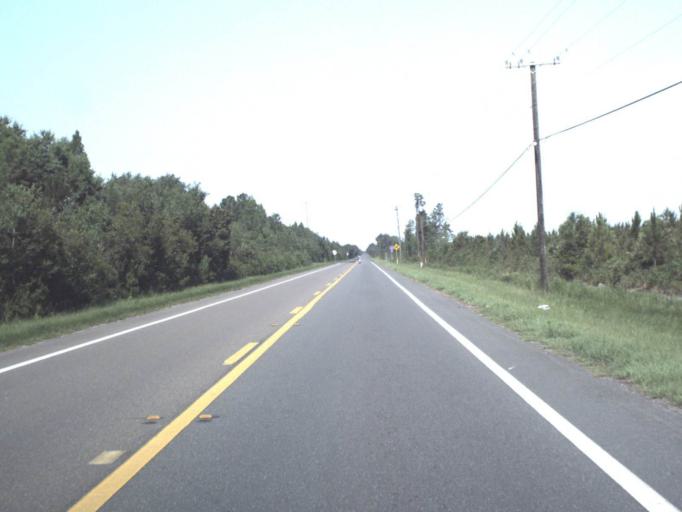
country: US
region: Florida
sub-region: Baker County
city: Macclenny
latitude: 30.2706
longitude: -82.1890
